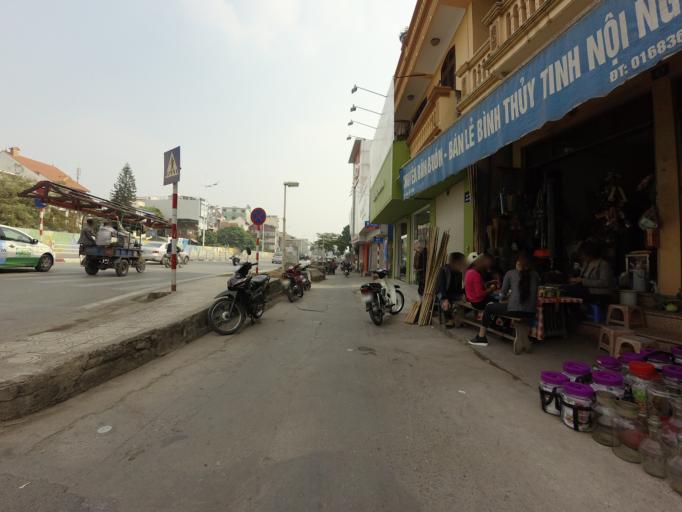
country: VN
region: Ha Noi
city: Tay Ho
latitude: 21.0609
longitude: 105.8328
